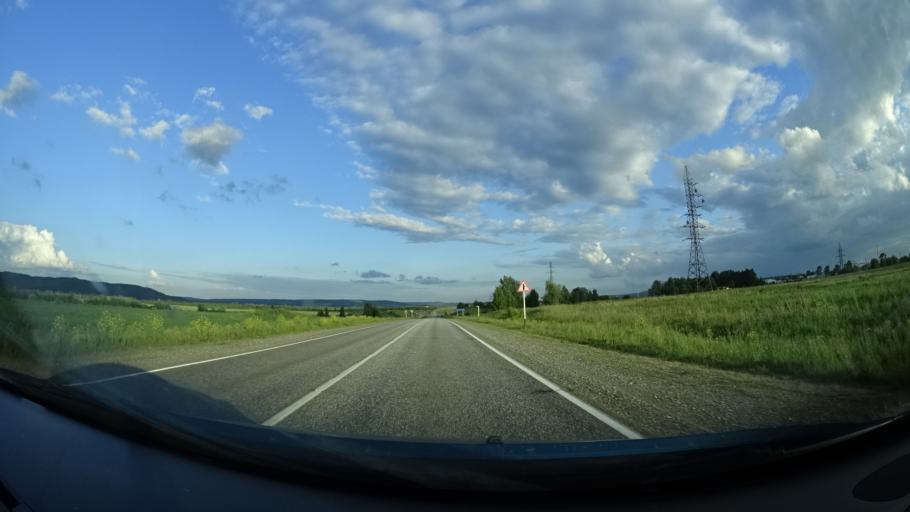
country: RU
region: Perm
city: Barda
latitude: 57.0954
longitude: 55.5333
